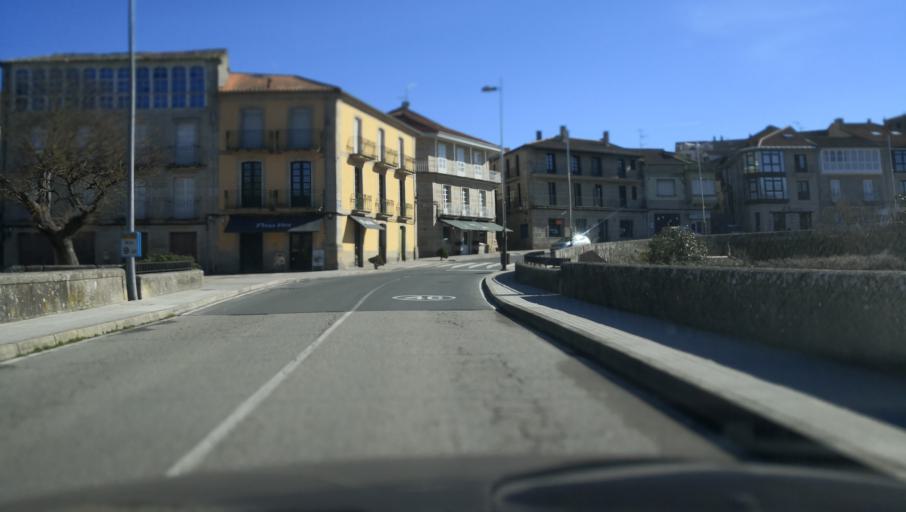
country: ES
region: Galicia
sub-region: Provincia de Ourense
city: Allariz
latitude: 42.1898
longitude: -7.8039
